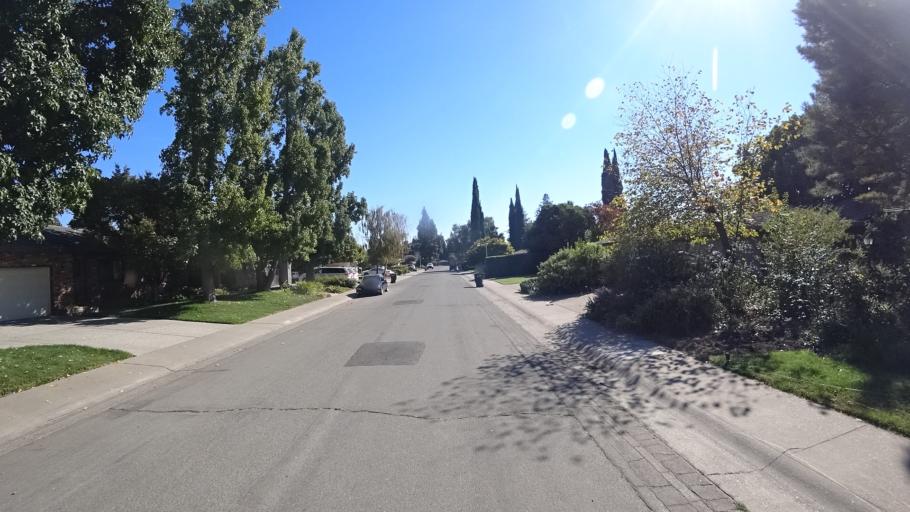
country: US
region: California
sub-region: Sacramento County
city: Parkway
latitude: 38.5043
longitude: -121.5238
